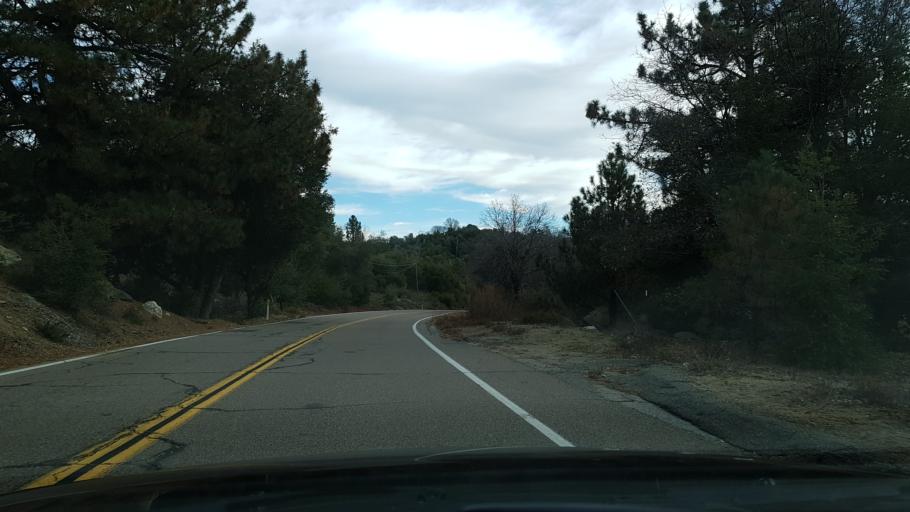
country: US
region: California
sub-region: Riverside County
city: Aguanga
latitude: 33.3573
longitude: -116.8709
